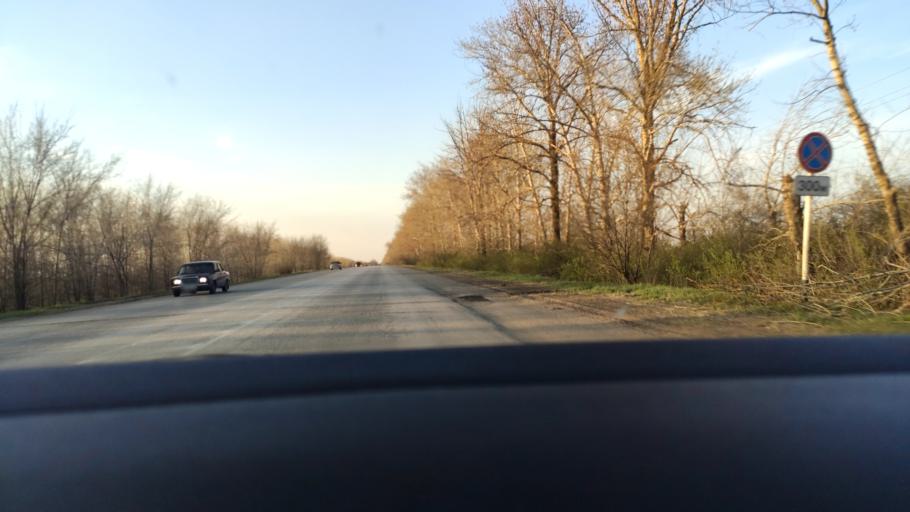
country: RU
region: Voronezj
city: Maslovka
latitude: 51.4602
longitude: 39.3047
